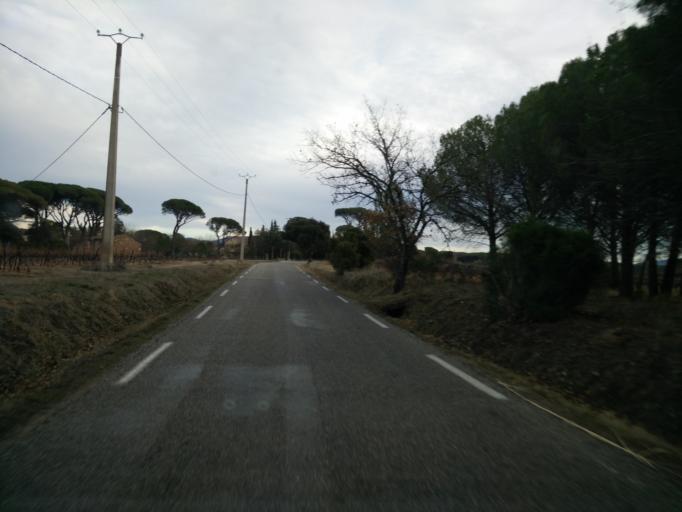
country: FR
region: Provence-Alpes-Cote d'Azur
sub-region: Departement du Var
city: Vidauban
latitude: 43.3983
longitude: 6.4320
